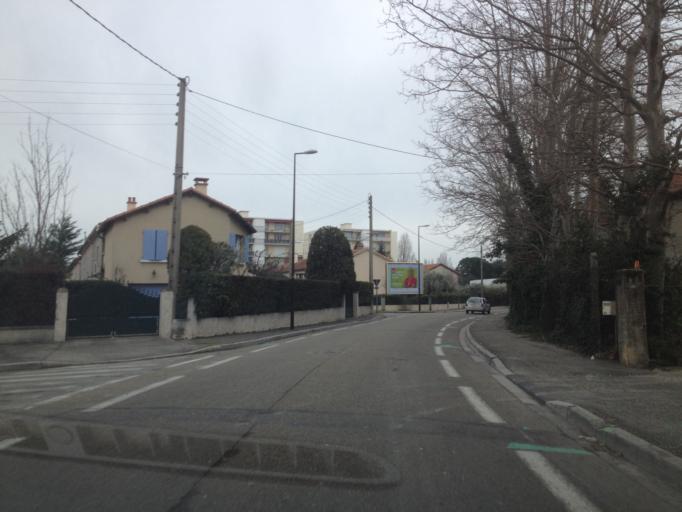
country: FR
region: Provence-Alpes-Cote d'Azur
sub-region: Departement du Vaucluse
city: Avignon
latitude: 43.9316
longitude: 4.8226
